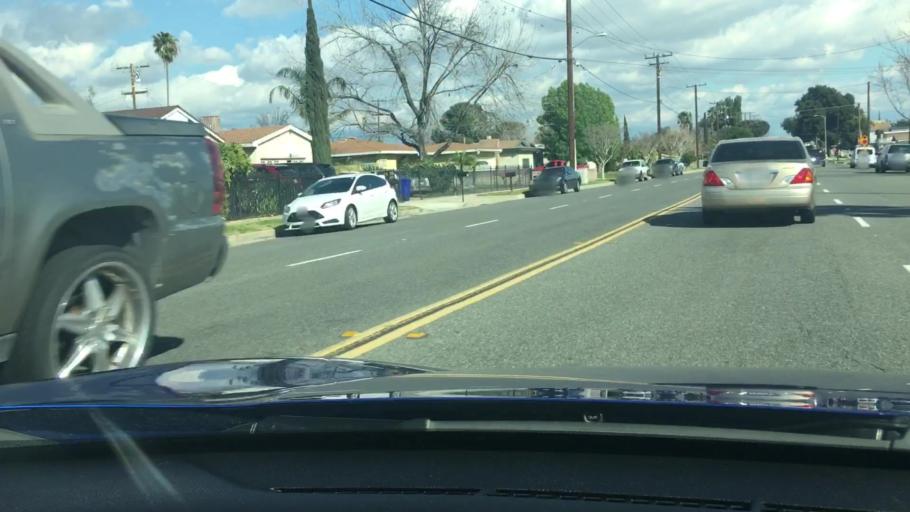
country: US
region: California
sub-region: San Bernardino County
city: Rialto
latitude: 34.0850
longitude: -117.3681
